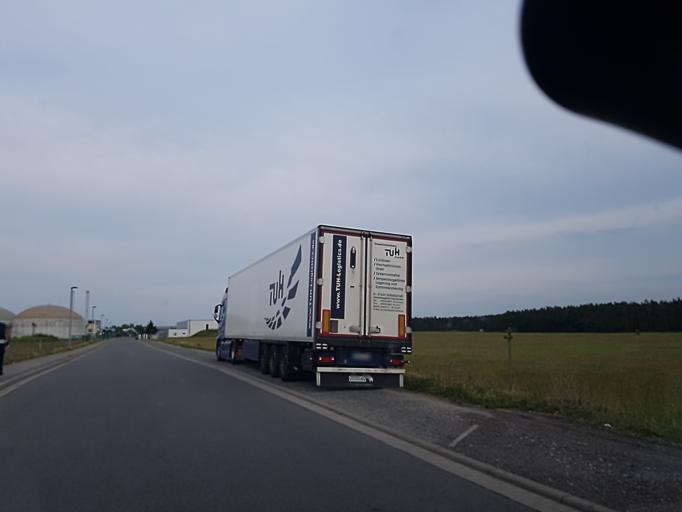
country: DE
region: Saxony-Anhalt
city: Jessen
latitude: 51.7986
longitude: 12.9316
